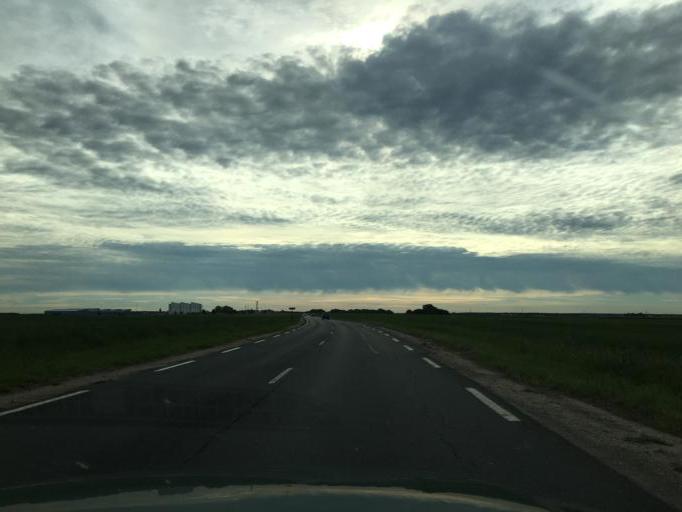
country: FR
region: Centre
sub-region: Departement du Loiret
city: Bricy
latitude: 47.9762
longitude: 1.7485
